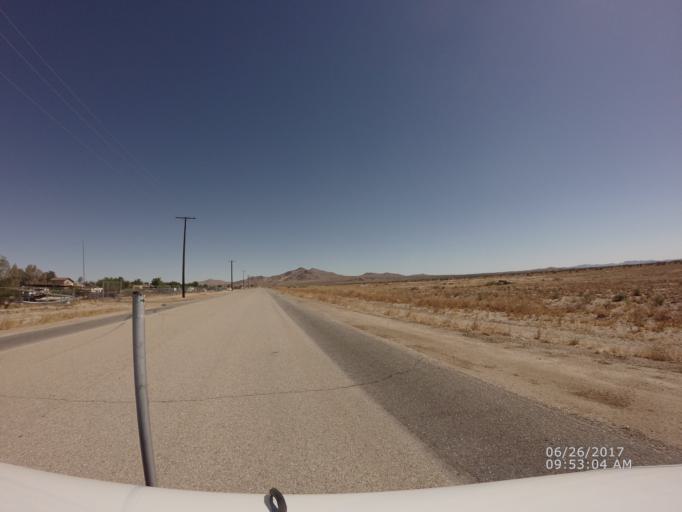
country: US
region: California
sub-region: Los Angeles County
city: Lake Los Angeles
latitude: 34.6252
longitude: -117.8093
